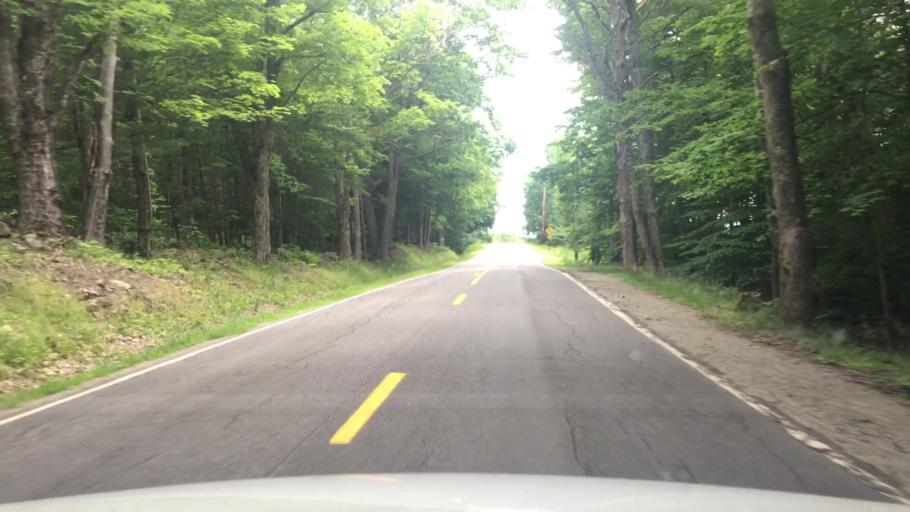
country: US
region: Maine
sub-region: Waldo County
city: Searsmont
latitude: 44.4449
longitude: -69.2940
